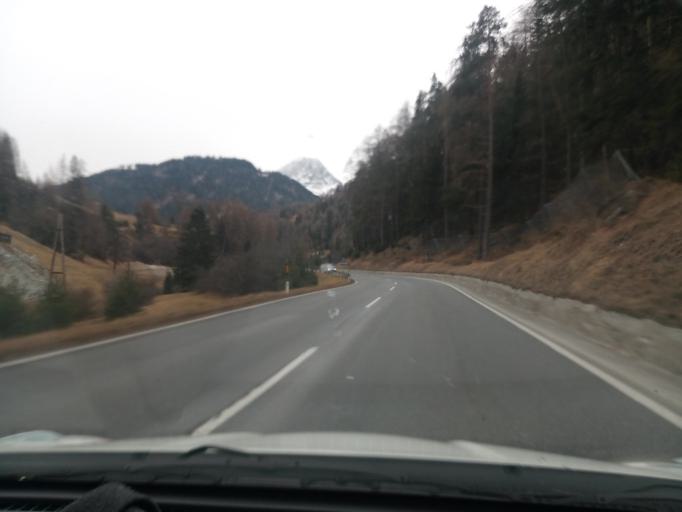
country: AT
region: Tyrol
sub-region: Politischer Bezirk Landeck
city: Nauders
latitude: 46.9064
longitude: 10.4946
